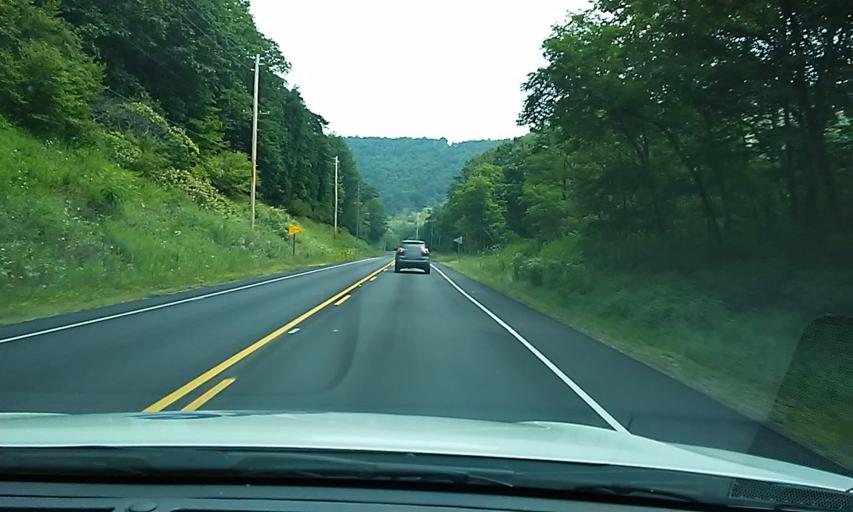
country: US
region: Pennsylvania
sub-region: Cameron County
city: Emporium
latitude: 41.4717
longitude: -78.3439
